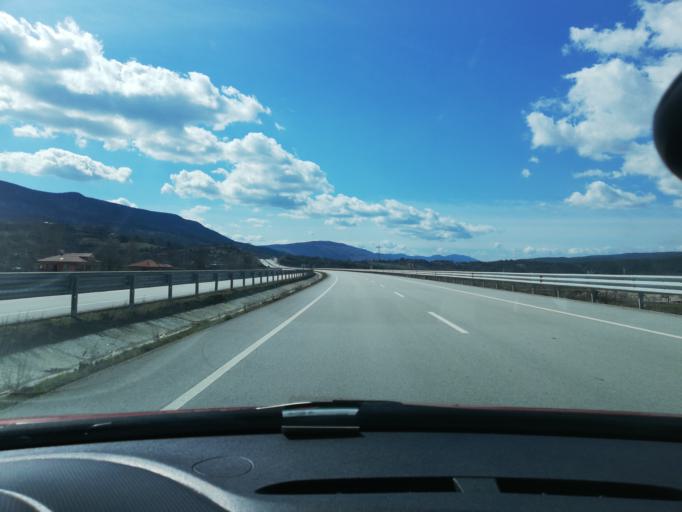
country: TR
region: Kastamonu
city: Igdir
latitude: 41.2287
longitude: 33.0078
